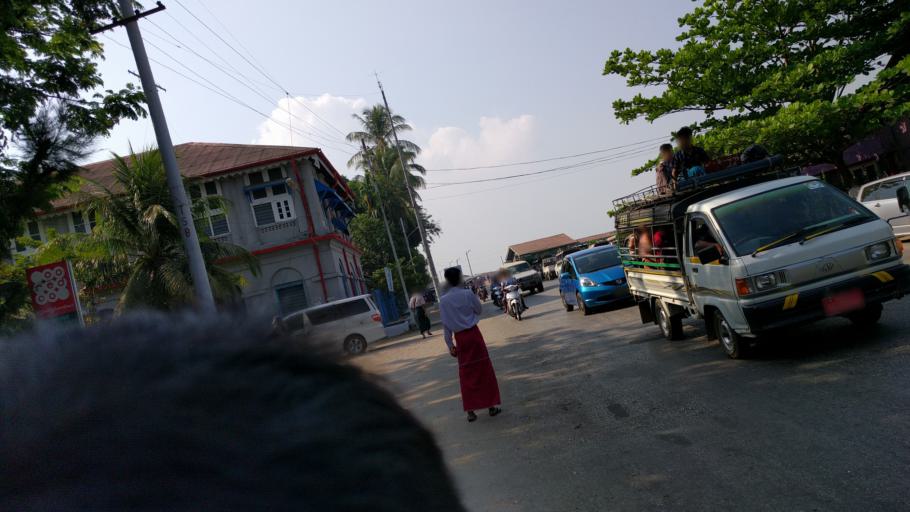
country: MM
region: Mon
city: Mawlamyine
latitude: 16.4841
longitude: 97.6185
